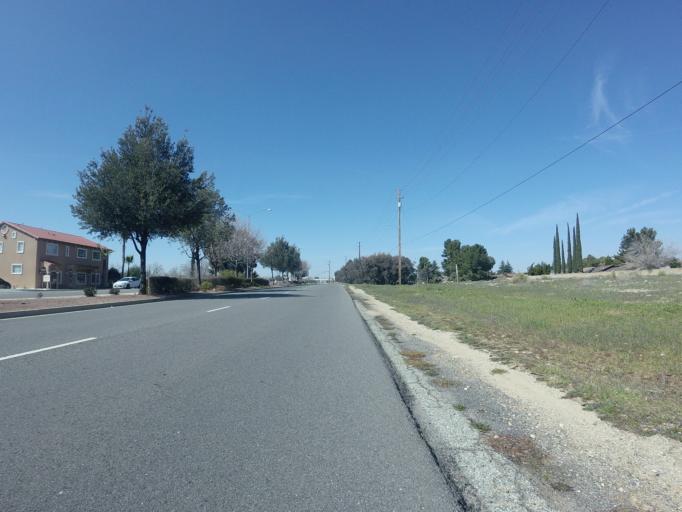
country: US
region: California
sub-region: Riverside County
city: Beaumont
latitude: 33.9287
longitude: -116.9355
